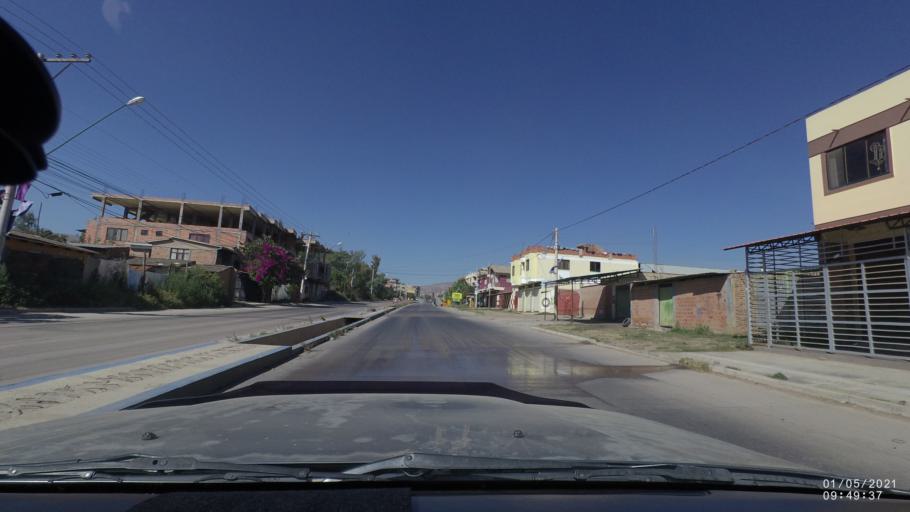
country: BO
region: Cochabamba
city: Cochabamba
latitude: -17.4573
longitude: -66.1680
